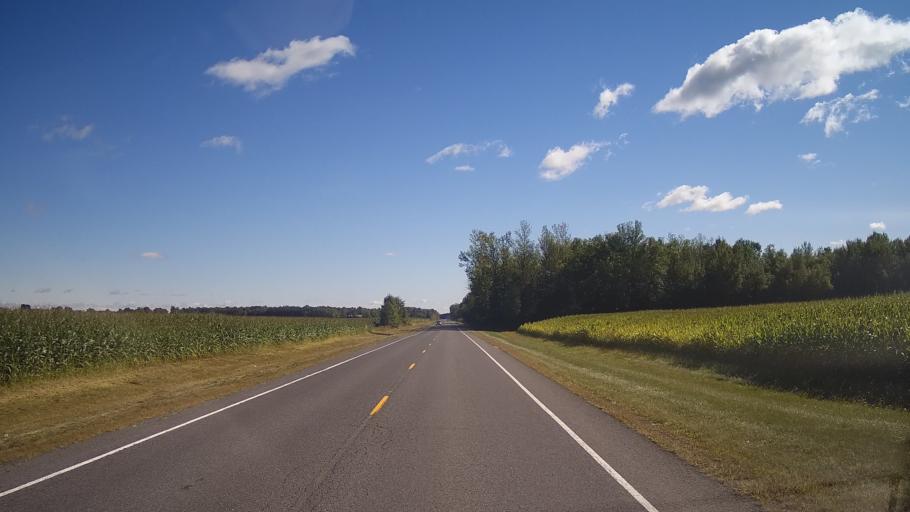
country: CA
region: Ontario
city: Prescott
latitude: 44.9072
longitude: -75.4362
